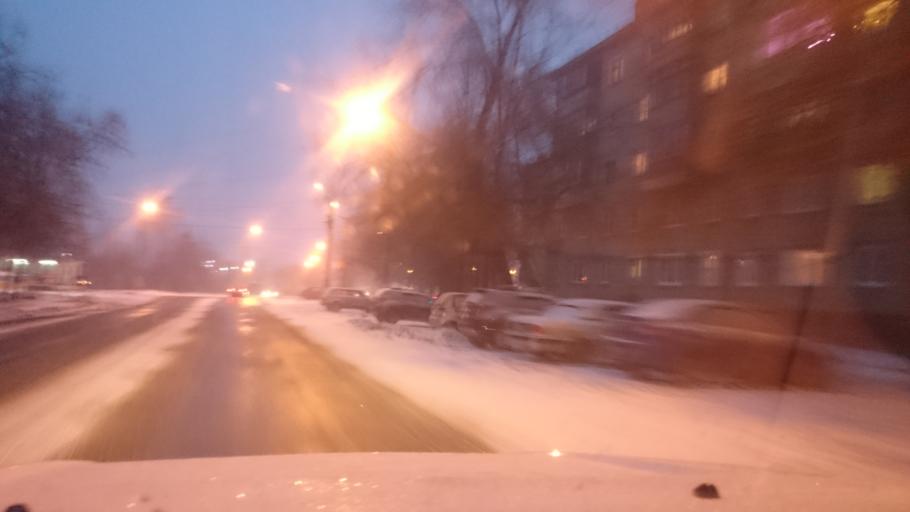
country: RU
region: Tula
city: Mendeleyevskiy
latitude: 54.1961
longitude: 37.5435
